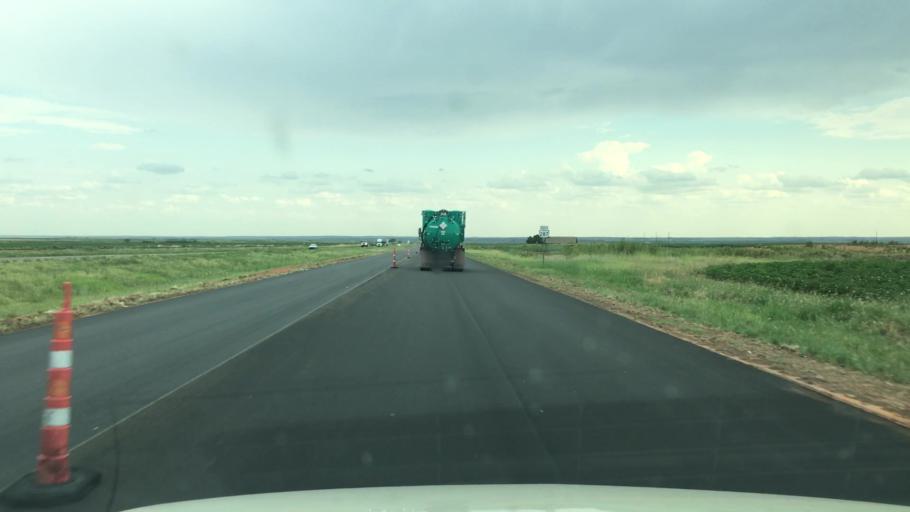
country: US
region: Texas
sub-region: Hall County
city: Memphis
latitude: 34.6237
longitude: -100.4735
